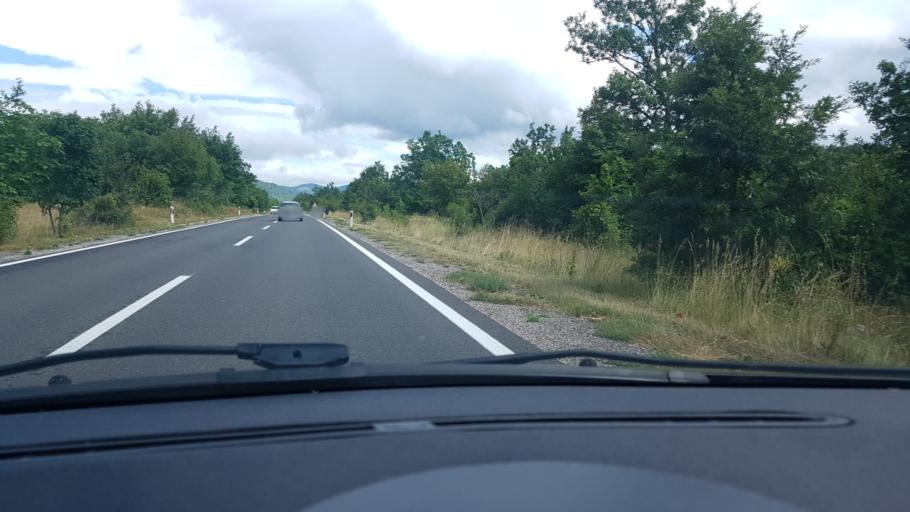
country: HR
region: Zadarska
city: Gracac
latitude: 44.4585
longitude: 15.8159
